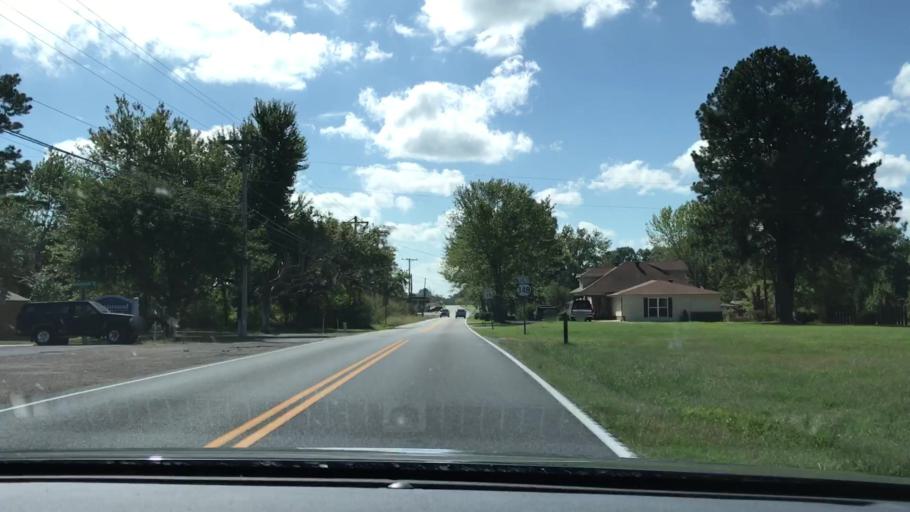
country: US
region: Kentucky
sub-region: McCracken County
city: Reidland
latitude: 36.9227
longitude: -88.5197
